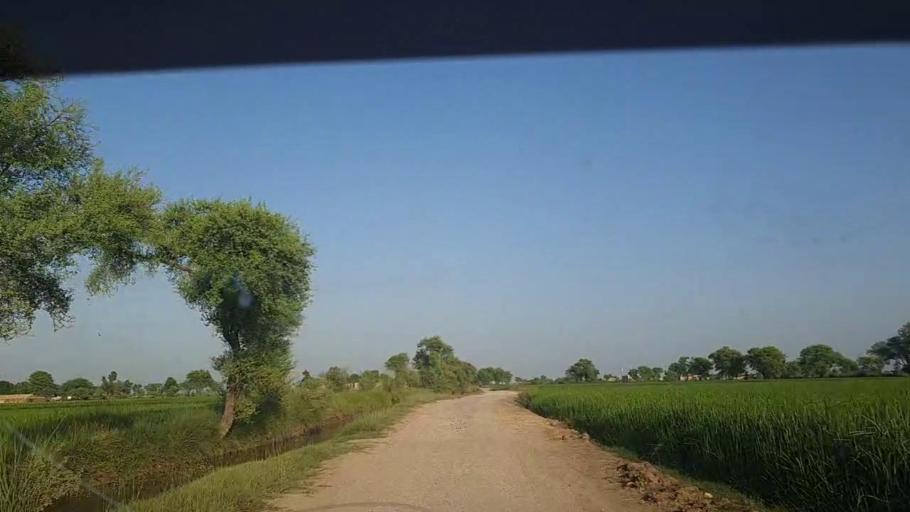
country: PK
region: Sindh
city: Thul
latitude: 28.2147
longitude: 68.8732
